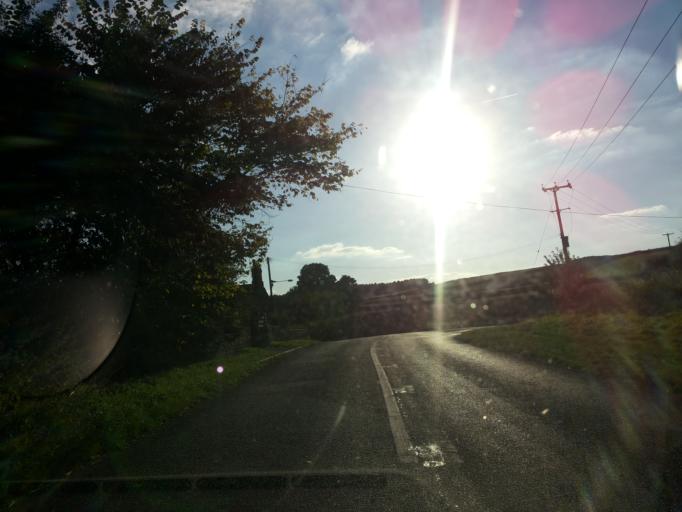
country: GB
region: England
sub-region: Derbyshire
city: Tibshelf
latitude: 53.1830
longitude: -1.3244
